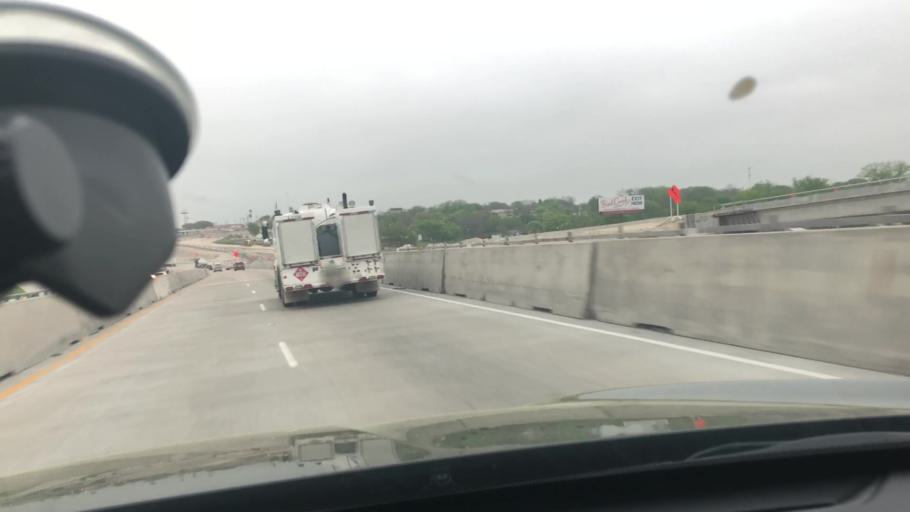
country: US
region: Texas
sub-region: Bell County
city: Temple
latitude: 31.0978
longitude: -97.3647
